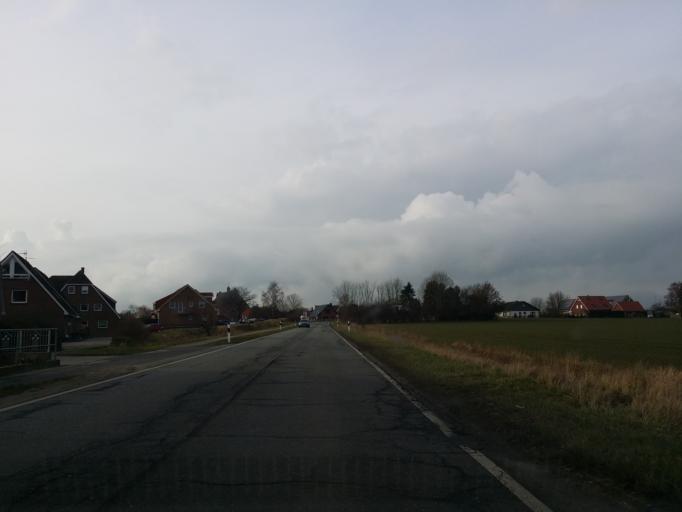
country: DE
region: Schleswig-Holstein
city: Fehmarn
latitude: 54.4495
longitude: 11.1523
